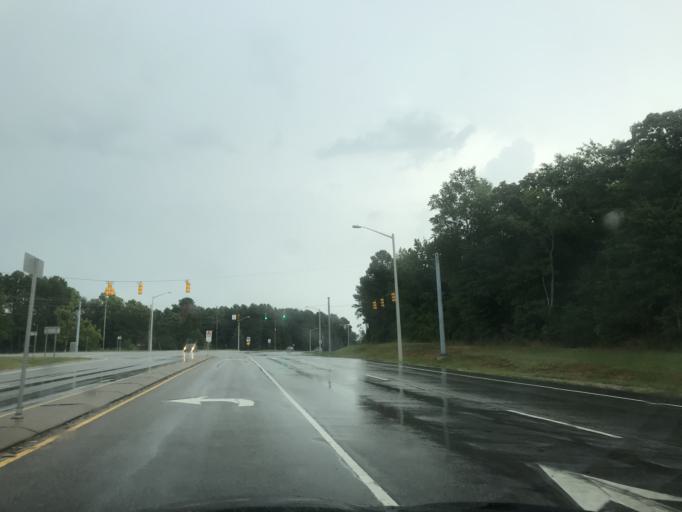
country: US
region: North Carolina
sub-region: Johnston County
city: Clayton
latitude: 35.6389
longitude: -78.4399
